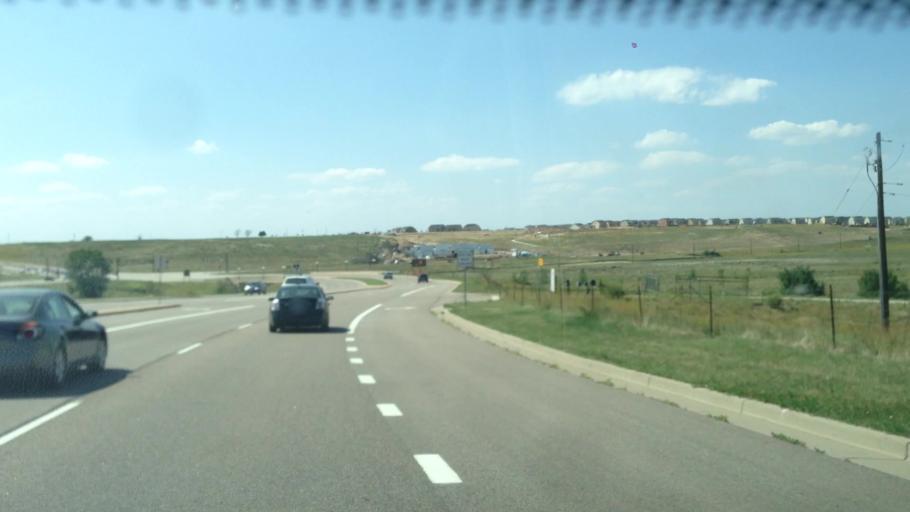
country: US
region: Colorado
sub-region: Douglas County
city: Stonegate
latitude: 39.5155
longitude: -104.8081
